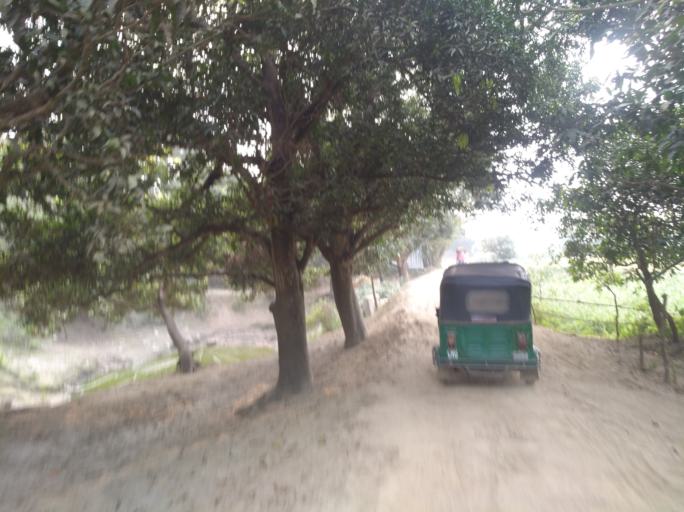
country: BD
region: Dhaka
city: Nagarpur
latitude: 24.0008
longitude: 89.7961
